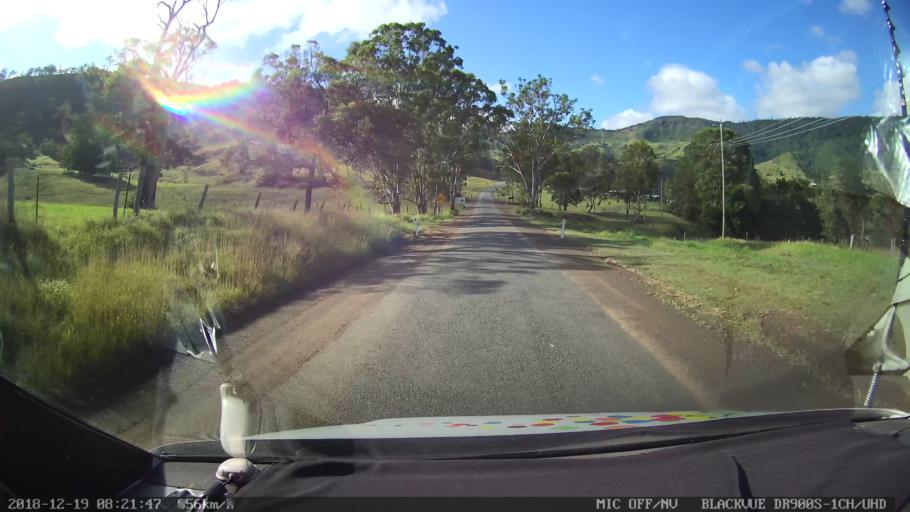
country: AU
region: New South Wales
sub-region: Kyogle
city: Kyogle
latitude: -28.2999
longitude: 152.9108
